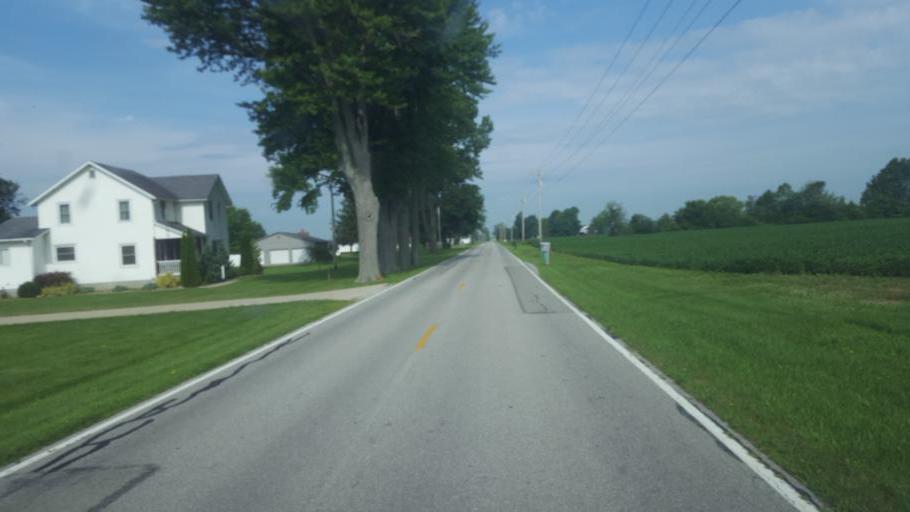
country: US
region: Ohio
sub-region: Marion County
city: Marion
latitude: 40.5635
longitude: -83.2327
